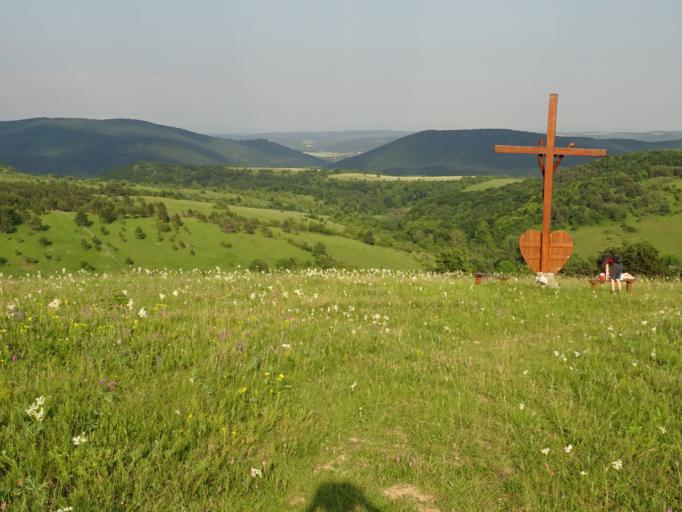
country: HU
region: Borsod-Abauj-Zemplen
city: Rudabanya
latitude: 48.4675
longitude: 20.6409
